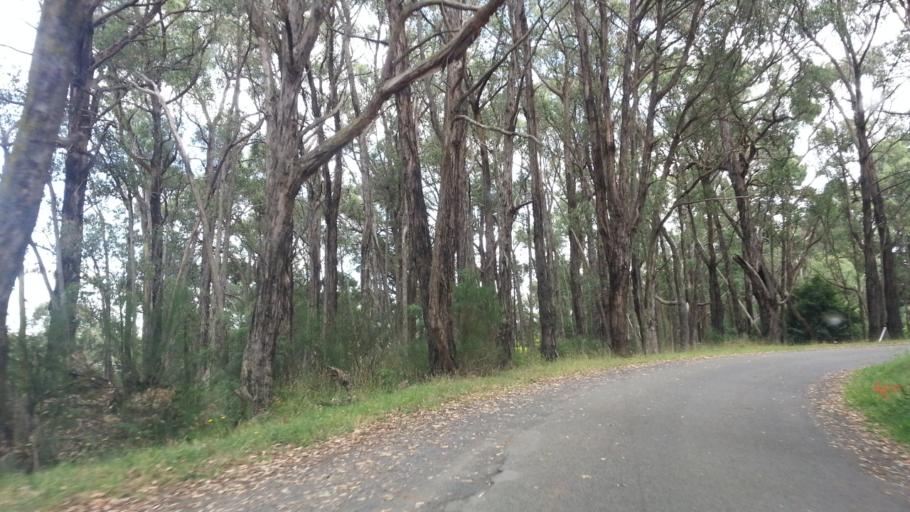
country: AU
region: Victoria
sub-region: Cardinia
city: Emerald
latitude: -37.9471
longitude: 145.4414
